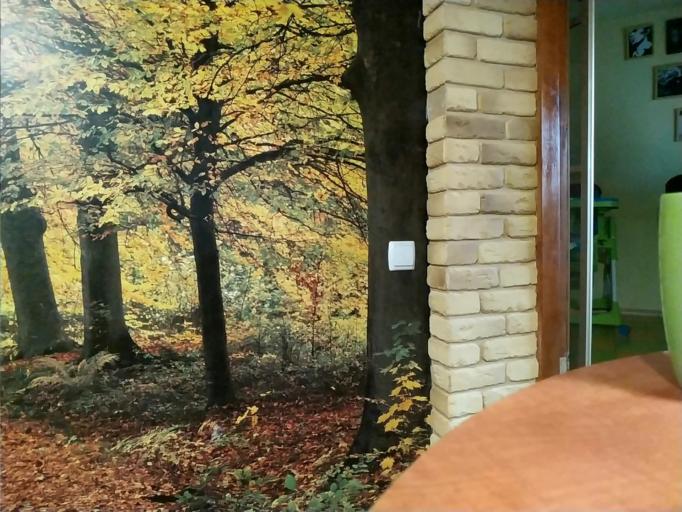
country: RU
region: Tverskaya
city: Staraya Toropa
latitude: 56.3501
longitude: 31.8171
